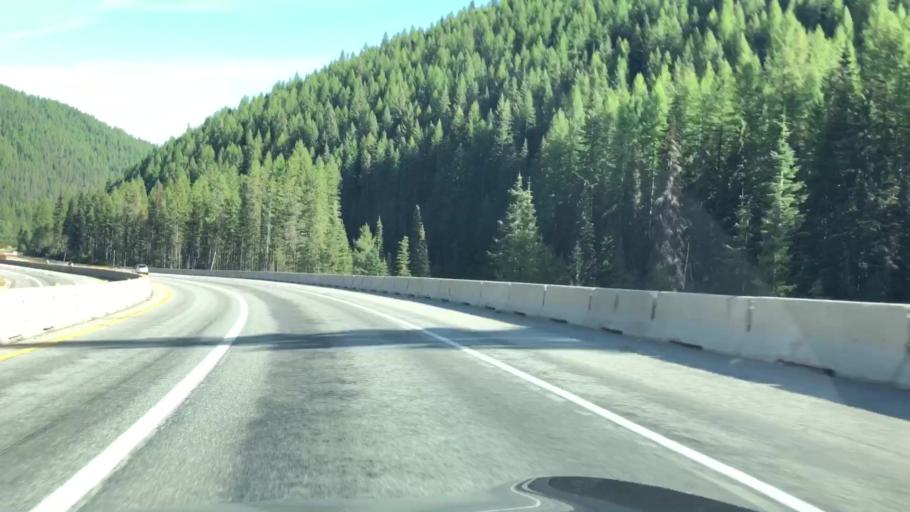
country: US
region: Idaho
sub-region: Shoshone County
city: Wallace
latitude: 47.4324
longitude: -115.6522
